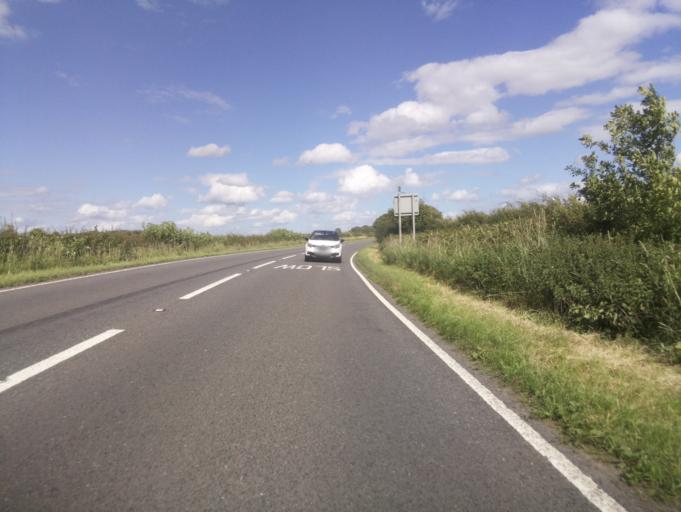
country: GB
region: England
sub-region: Nottinghamshire
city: Sutton Bonington
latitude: 52.8173
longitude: -1.2250
